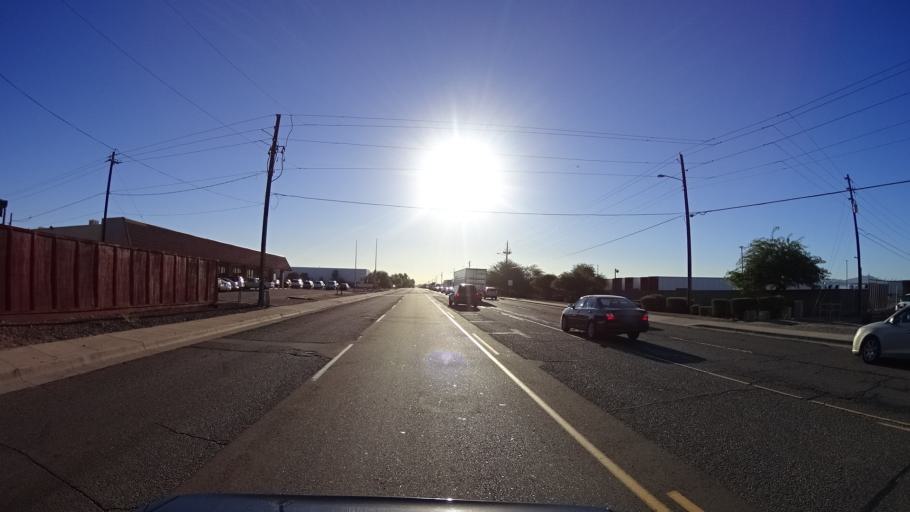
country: US
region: Arizona
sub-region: Maricopa County
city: Laveen
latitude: 33.4370
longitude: -112.1824
